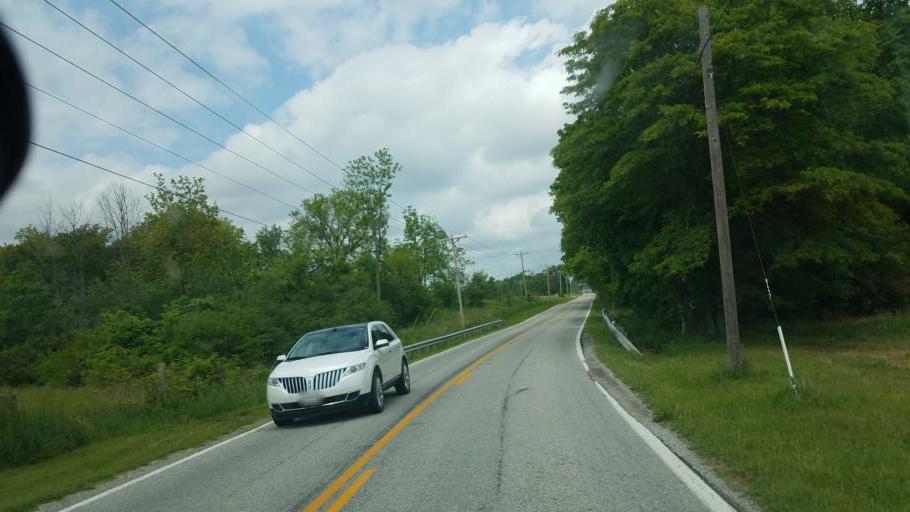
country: US
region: Ohio
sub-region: Marion County
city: Prospect
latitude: 40.4138
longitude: -83.1989
